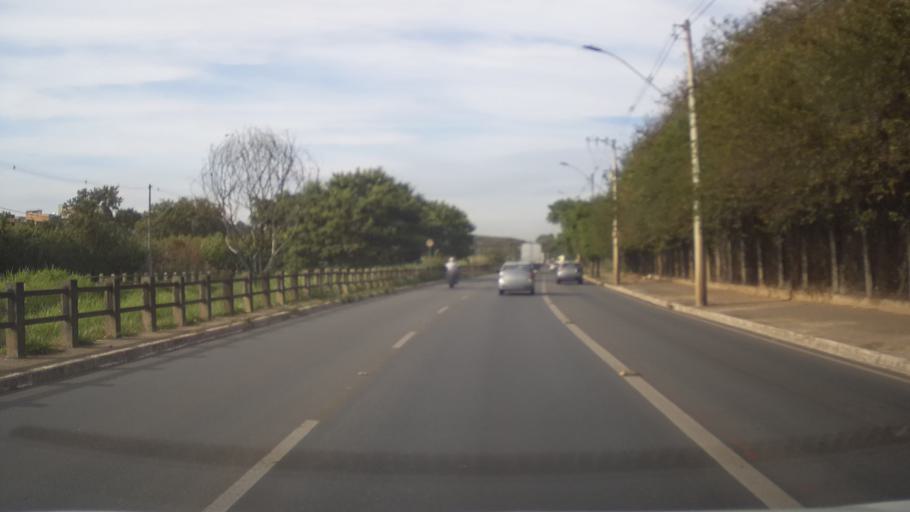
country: BR
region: Minas Gerais
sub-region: Contagem
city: Contagem
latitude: -19.8895
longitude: -44.0385
